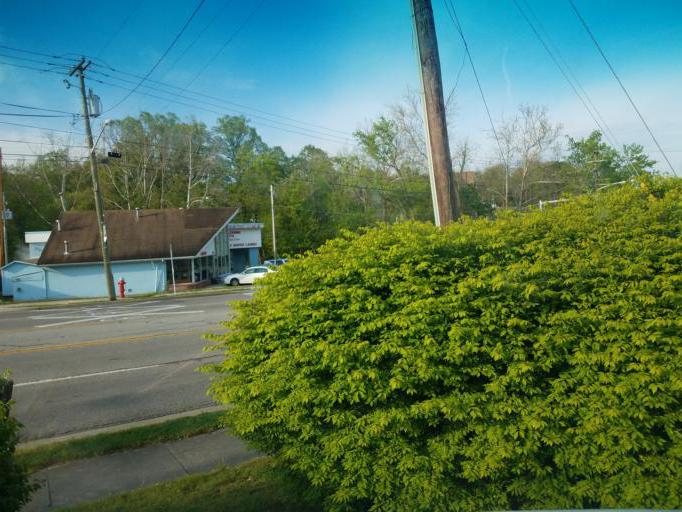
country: US
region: Virginia
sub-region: Smyth County
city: Marion
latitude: 36.8394
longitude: -81.5116
